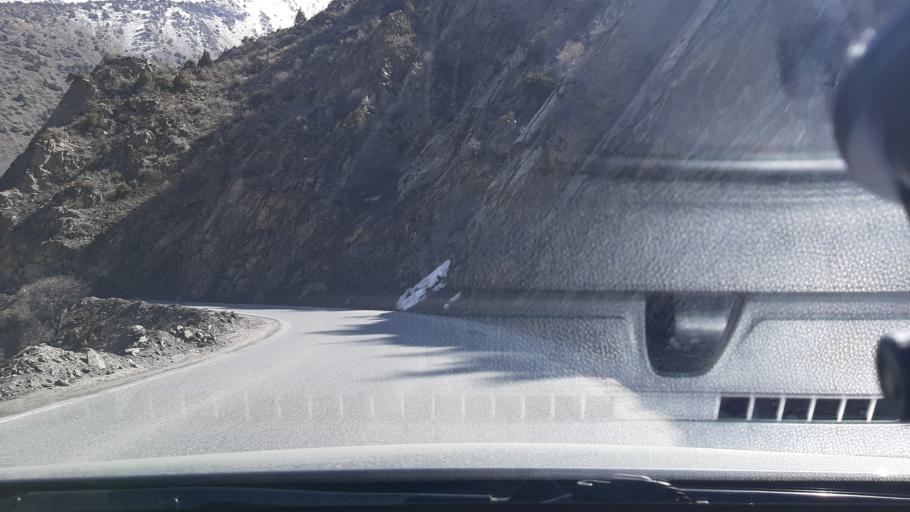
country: TJ
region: Viloyati Sughd
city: Ayni
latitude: 39.4900
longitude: 68.5514
